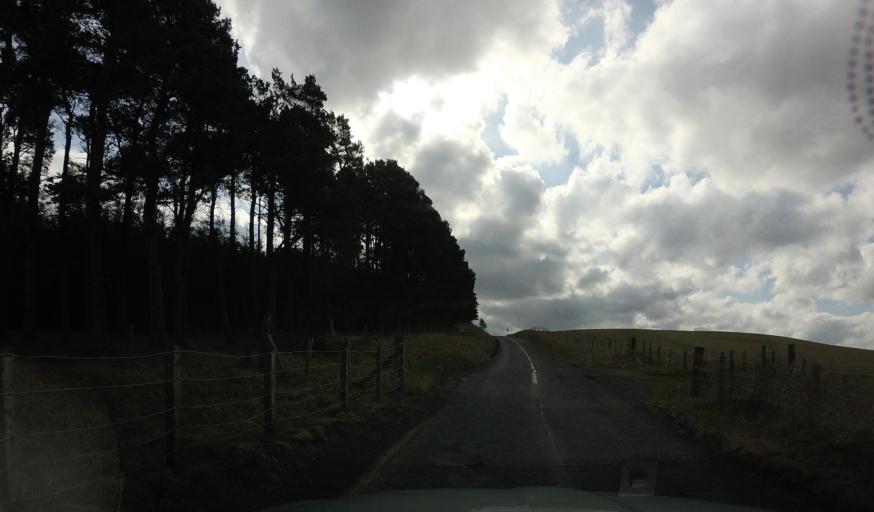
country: GB
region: Scotland
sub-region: Midlothian
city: Loanhead
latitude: 55.7955
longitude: -3.1454
